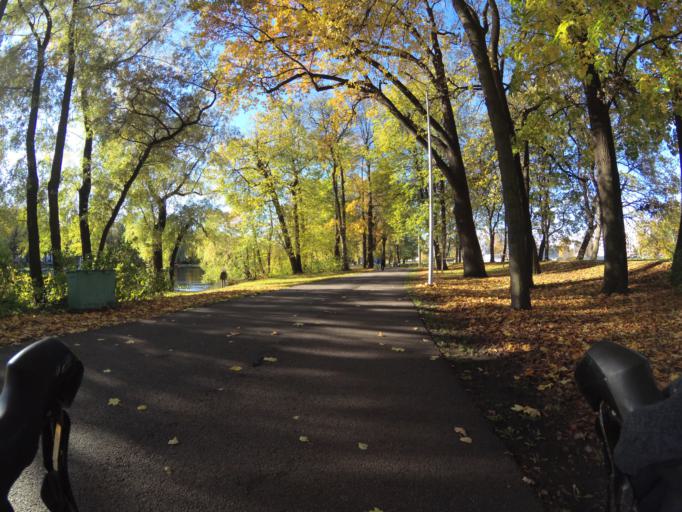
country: RU
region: Leningrad
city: Krestovskiy ostrov
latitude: 59.9818
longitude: 30.2536
